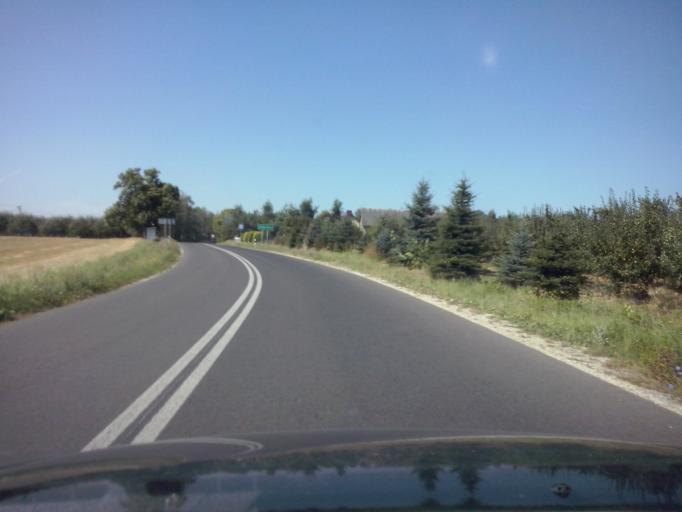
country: PL
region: Swietokrzyskie
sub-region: Powiat staszowski
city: Szydlow
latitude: 50.5870
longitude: 20.9671
